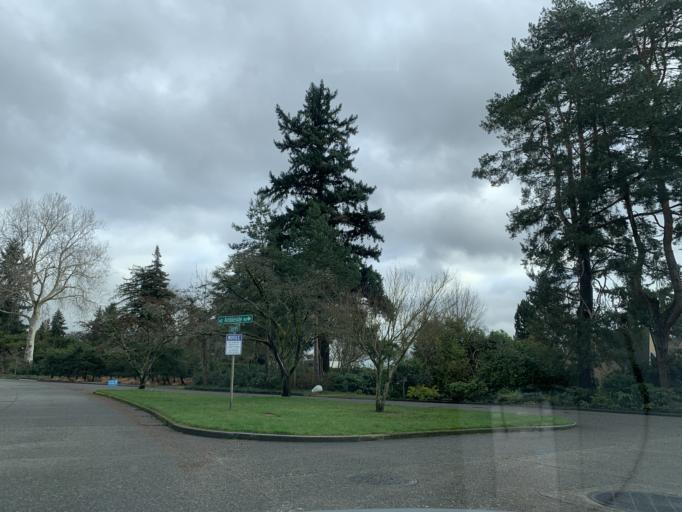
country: US
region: Washington
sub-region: King County
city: Yarrow Point
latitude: 47.6669
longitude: -122.2643
